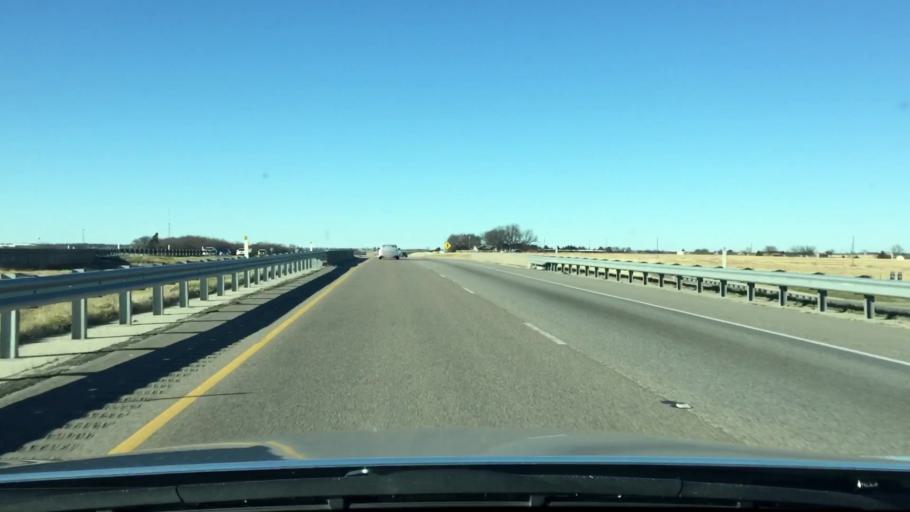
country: US
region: Texas
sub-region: Johnson County
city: Grandview
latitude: 32.2298
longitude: -97.1538
